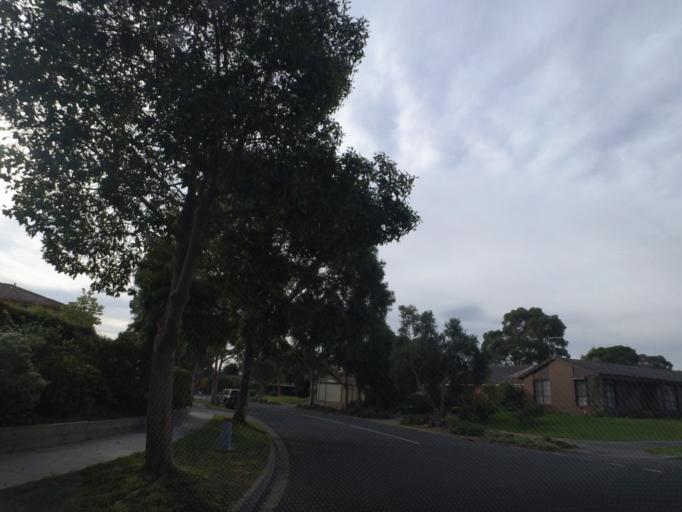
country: AU
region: Victoria
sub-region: Knox
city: Knoxfield
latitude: -37.8781
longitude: 145.2465
